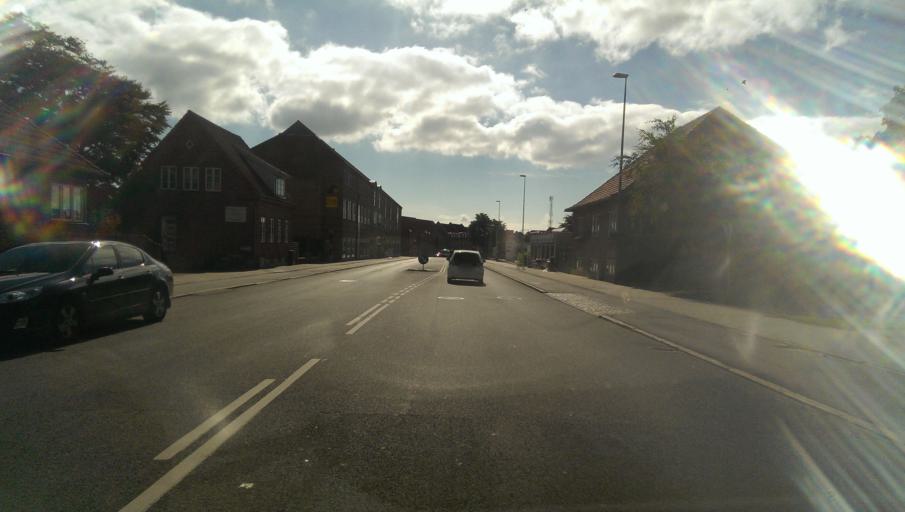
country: DK
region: South Denmark
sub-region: Esbjerg Kommune
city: Esbjerg
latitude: 55.4717
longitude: 8.4677
